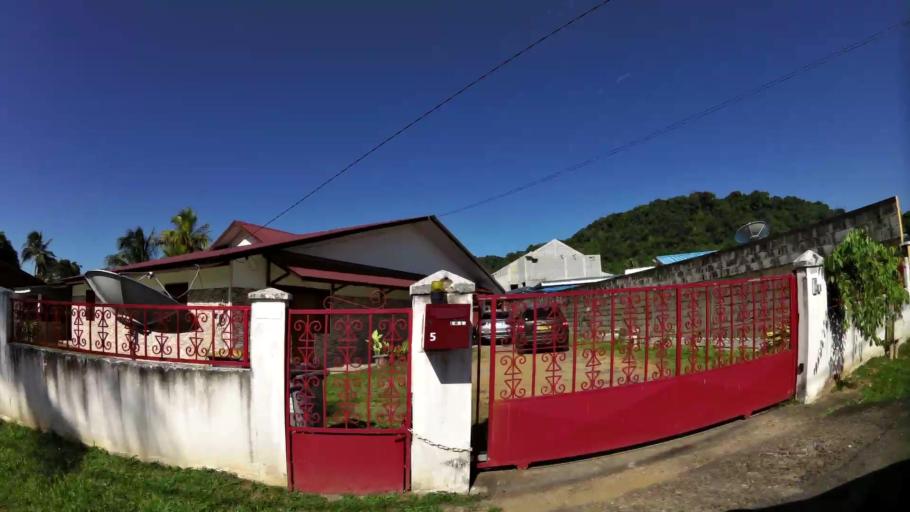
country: GF
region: Guyane
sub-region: Guyane
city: Remire-Montjoly
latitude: 4.8822
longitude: -52.2785
